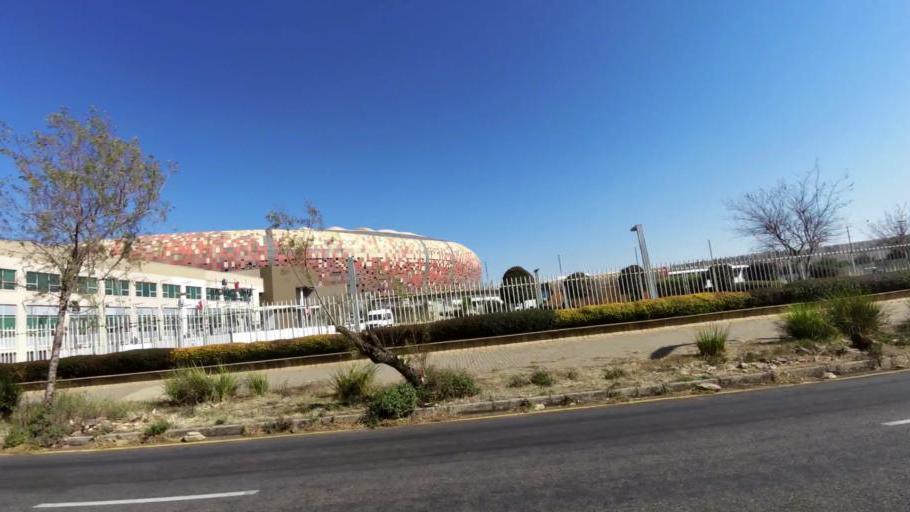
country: ZA
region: Gauteng
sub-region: City of Johannesburg Metropolitan Municipality
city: Johannesburg
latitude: -26.2333
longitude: 27.9854
